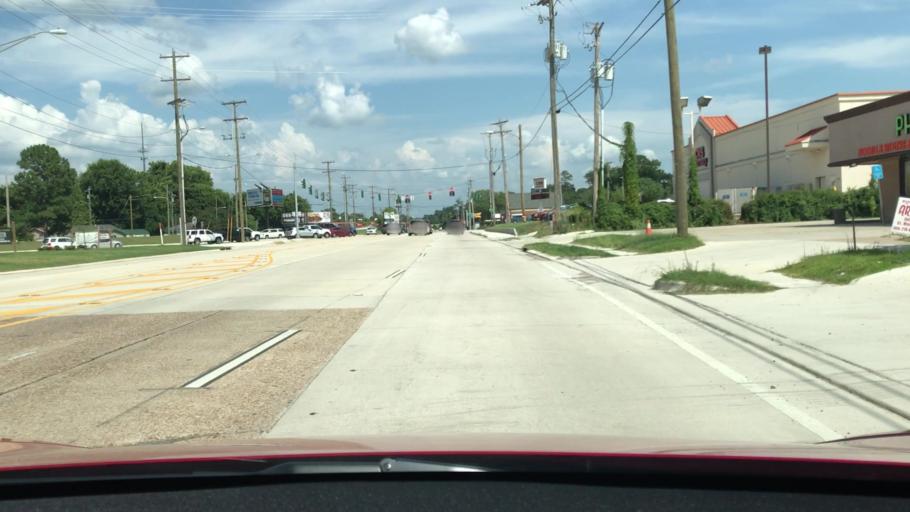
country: US
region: Louisiana
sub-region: Bossier Parish
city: Bossier City
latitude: 32.4806
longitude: -93.7237
